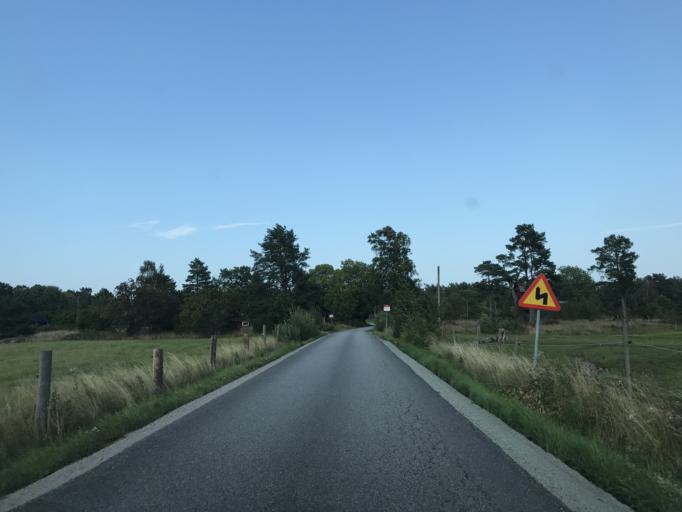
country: SE
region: Stockholm
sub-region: Norrtalje Kommun
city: Bjorko
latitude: 59.8558
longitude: 19.0204
